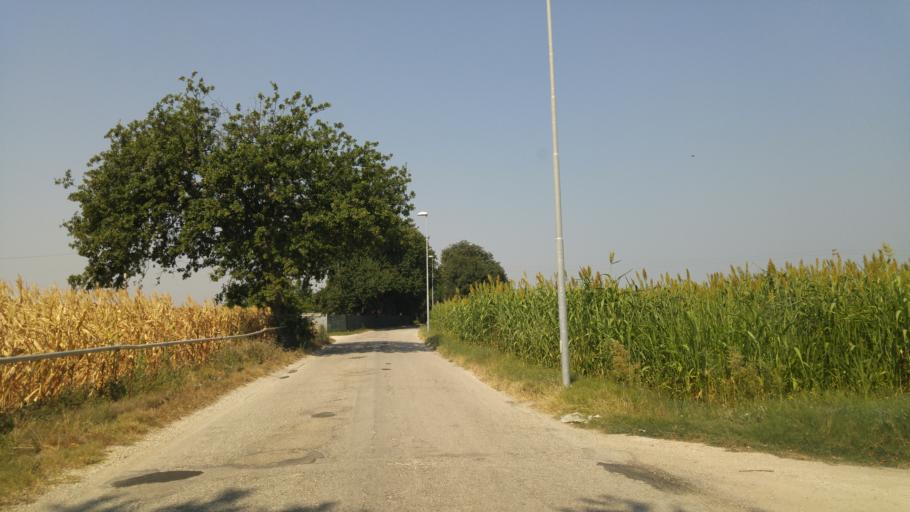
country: IT
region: The Marches
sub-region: Provincia di Pesaro e Urbino
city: Fano
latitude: 43.8313
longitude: 13.0364
